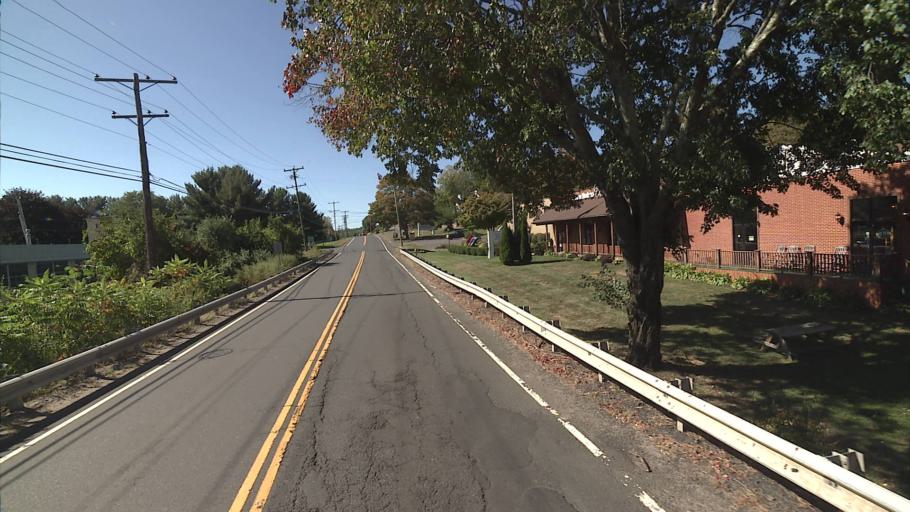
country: US
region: Connecticut
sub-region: New Haven County
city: Wolcott
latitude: 41.5746
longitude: -73.0014
